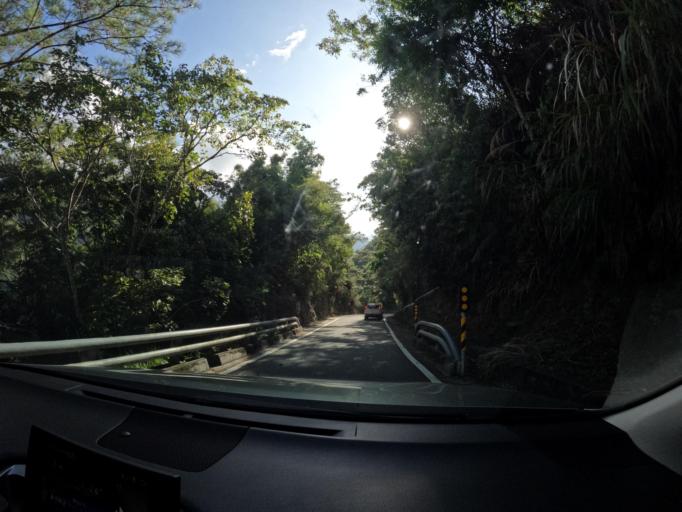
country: TW
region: Taiwan
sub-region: Taitung
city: Taitung
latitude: 23.1766
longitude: 121.0368
